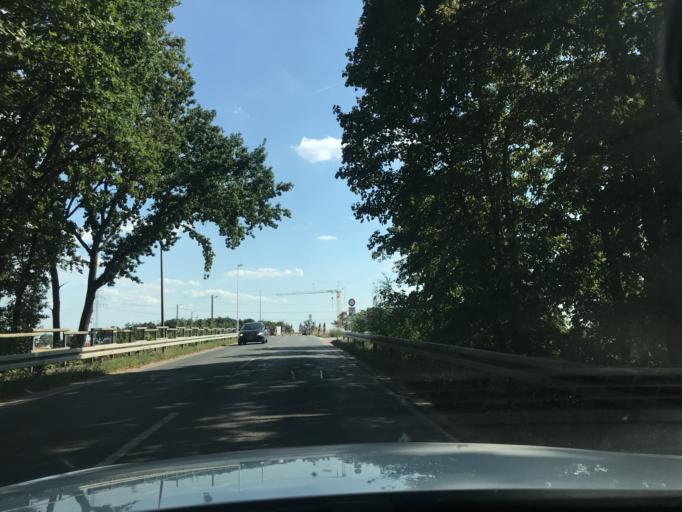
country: DE
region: Bavaria
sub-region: Regierungsbezirk Mittelfranken
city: Erlangen
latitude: 49.5620
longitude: 10.9866
